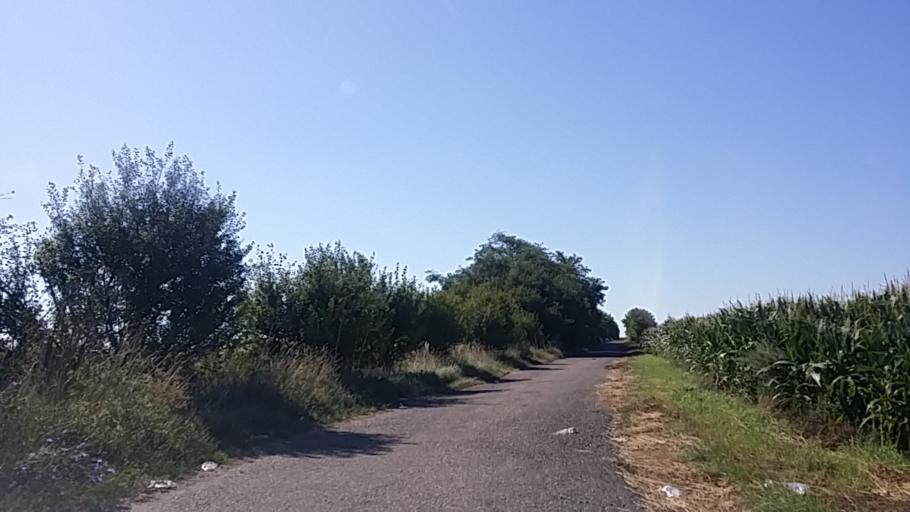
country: HU
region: Fejer
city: Mezofalva
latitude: 46.8944
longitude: 18.7095
